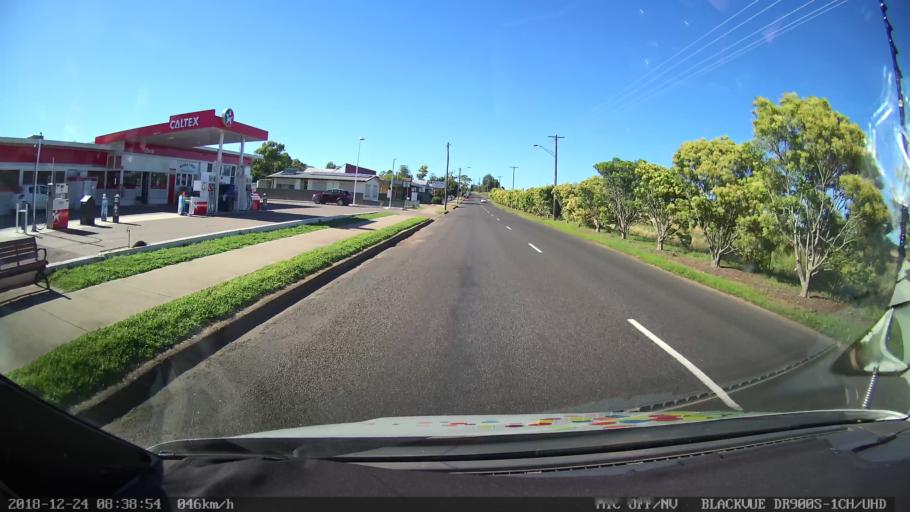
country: AU
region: New South Wales
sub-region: Liverpool Plains
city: Quirindi
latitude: -31.3443
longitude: 150.6475
